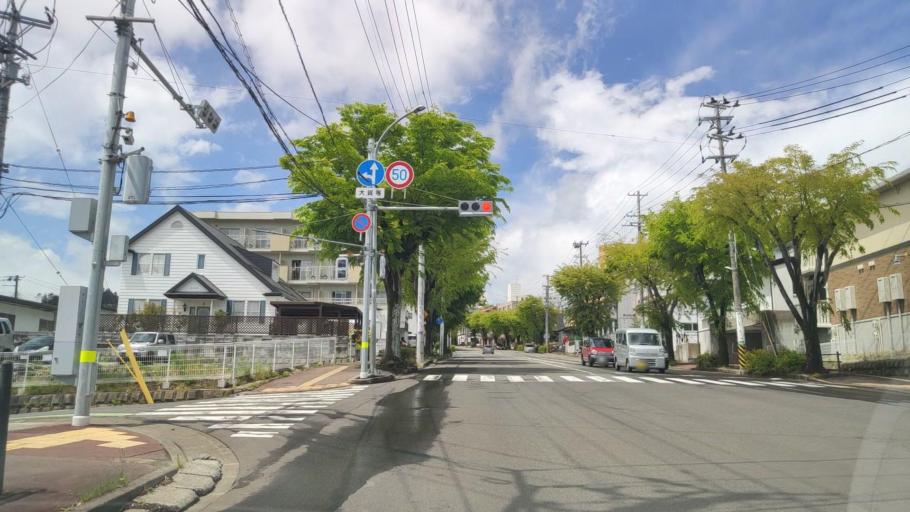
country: JP
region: Miyagi
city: Sendai
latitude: 38.2394
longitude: 140.8473
